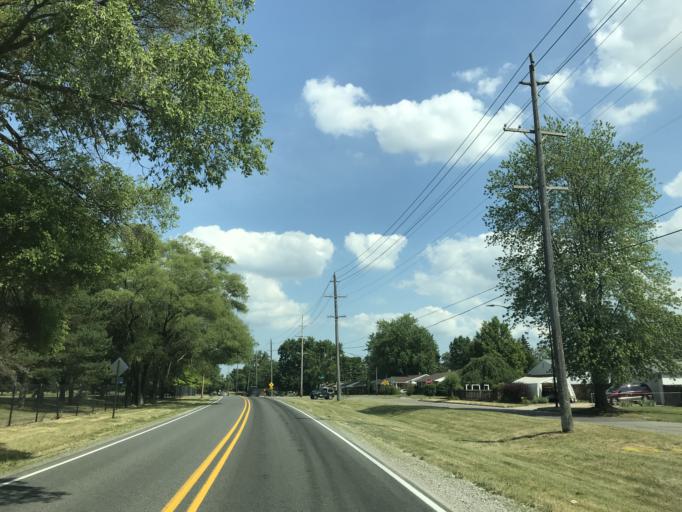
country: US
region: Michigan
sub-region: Washtenaw County
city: Ypsilanti
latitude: 42.2591
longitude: -83.5824
